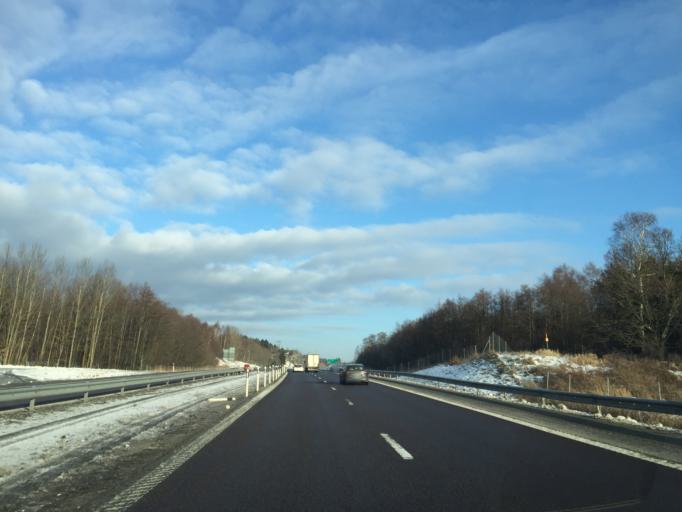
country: SE
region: Vaestra Goetaland
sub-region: Stenungsunds Kommun
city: Stora Hoga
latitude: 58.0324
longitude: 11.8465
